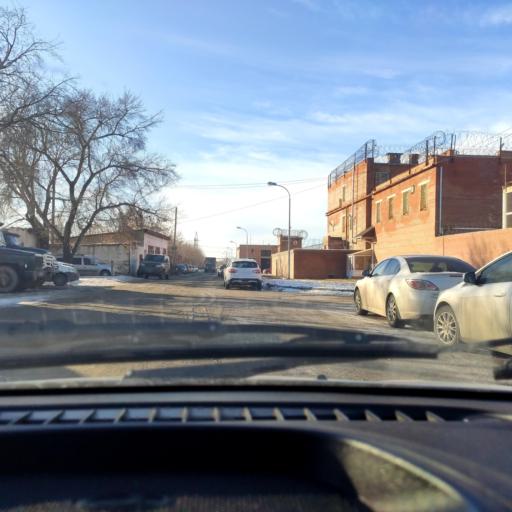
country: RU
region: Samara
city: Tol'yatti
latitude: 53.5746
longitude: 49.3454
